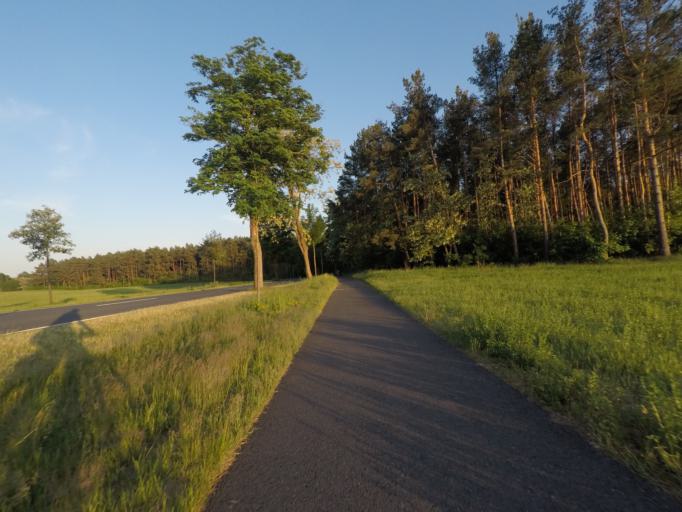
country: DE
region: Brandenburg
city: Marienwerder
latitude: 52.8618
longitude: 13.6475
